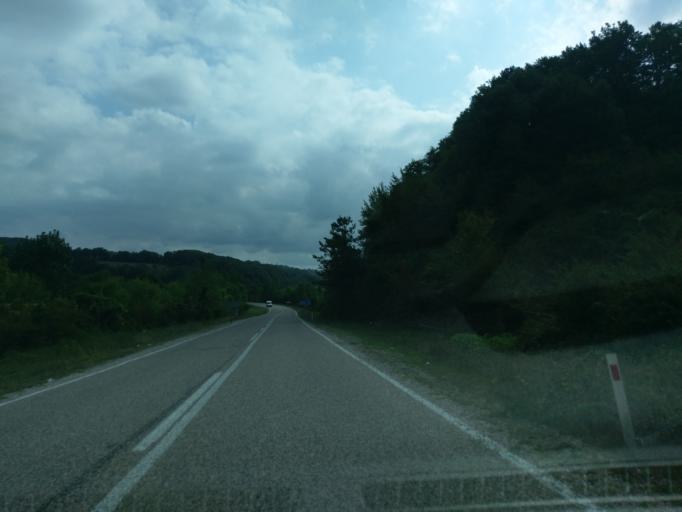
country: TR
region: Sinop
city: Erfelek
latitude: 41.9598
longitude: 34.8318
